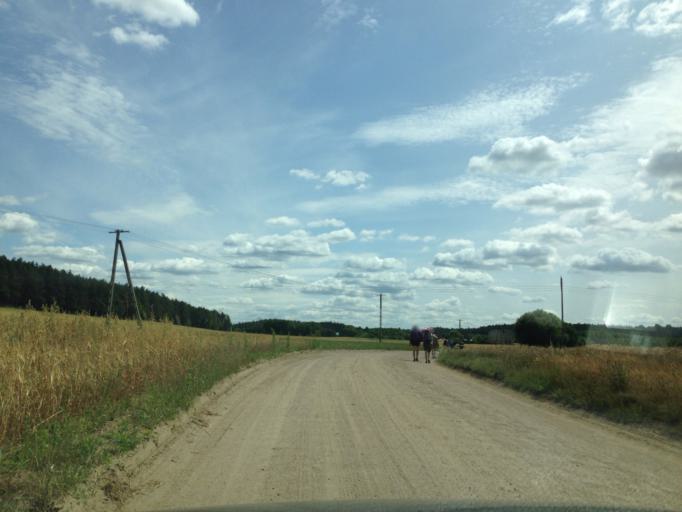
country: PL
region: Kujawsko-Pomorskie
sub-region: Powiat brodnicki
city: Bartniczka
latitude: 53.2589
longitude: 19.5888
